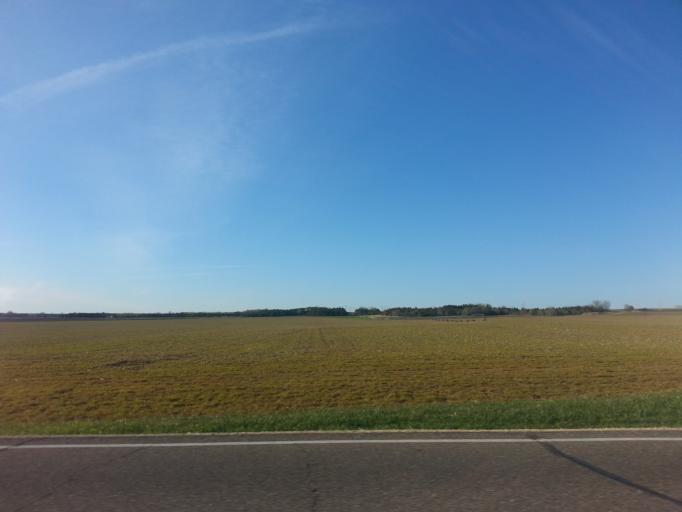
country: US
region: Minnesota
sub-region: Dakota County
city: Farmington
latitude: 44.5435
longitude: -93.0469
